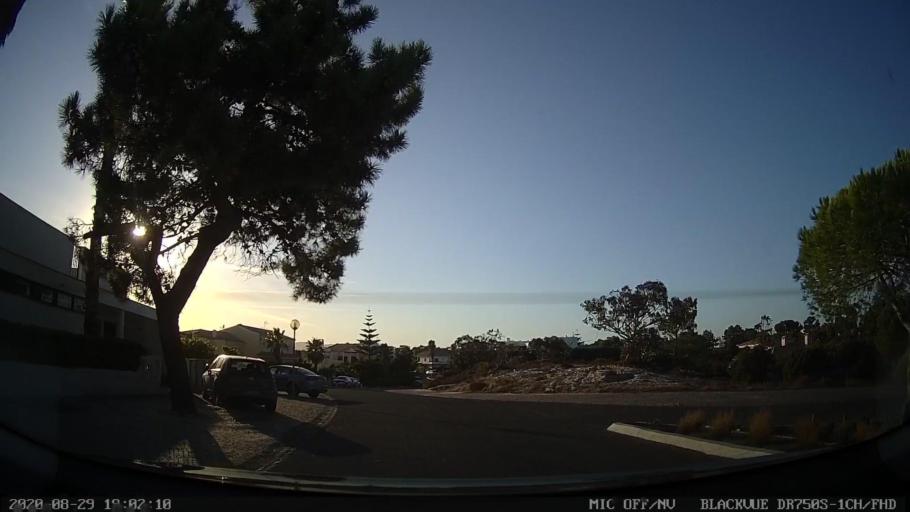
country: PT
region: Setubal
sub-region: Setubal
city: Setubal
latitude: 38.4543
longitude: -8.8613
